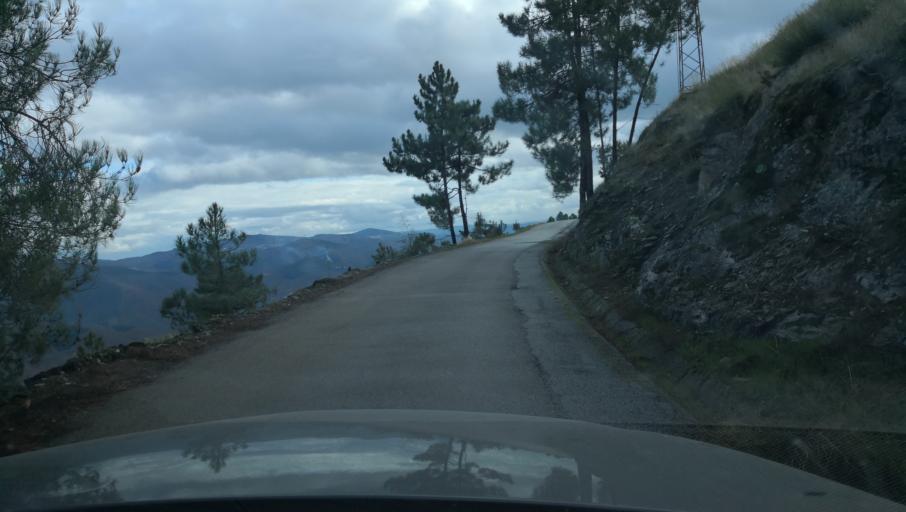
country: PT
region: Vila Real
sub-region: Sabrosa
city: Vilela
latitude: 41.1940
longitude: -7.5724
